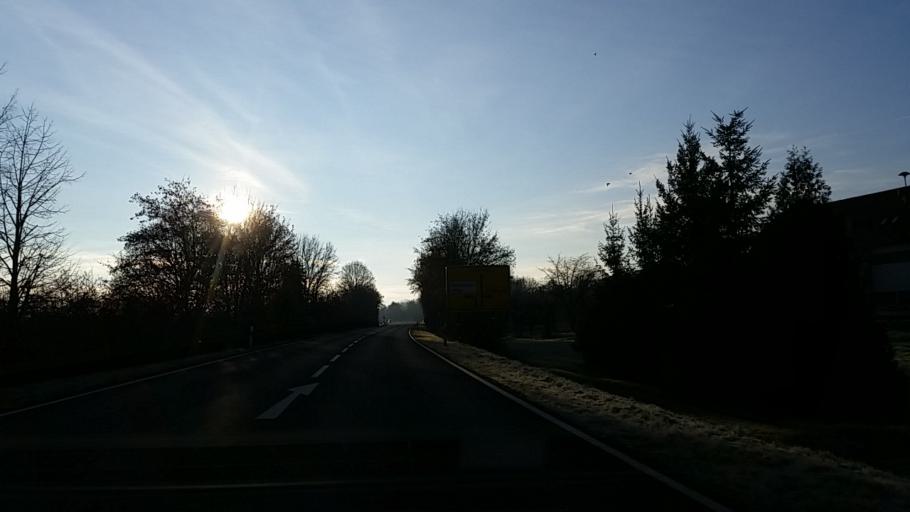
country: DE
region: Bavaria
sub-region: Regierungsbezirk Unterfranken
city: Erlabrunn
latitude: 49.8573
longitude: 9.8487
